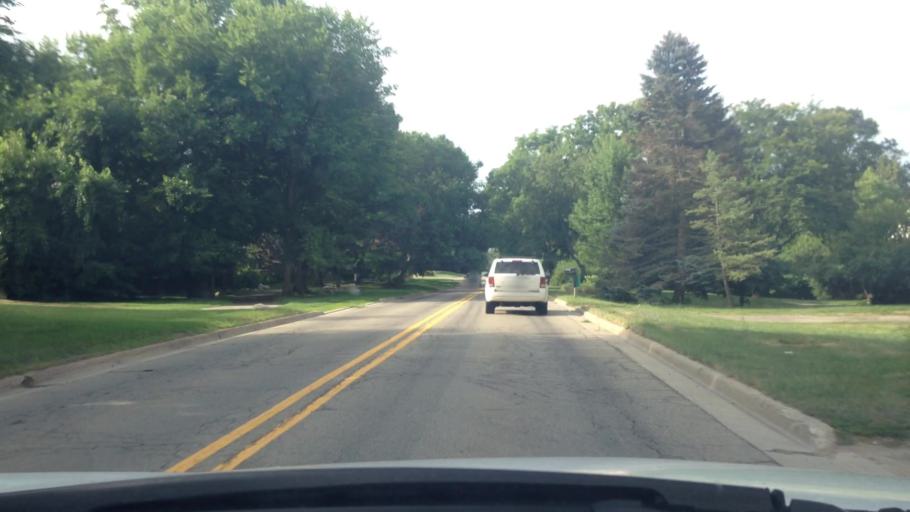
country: US
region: Michigan
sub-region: Oakland County
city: Clarkston
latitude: 42.7446
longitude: -83.3505
